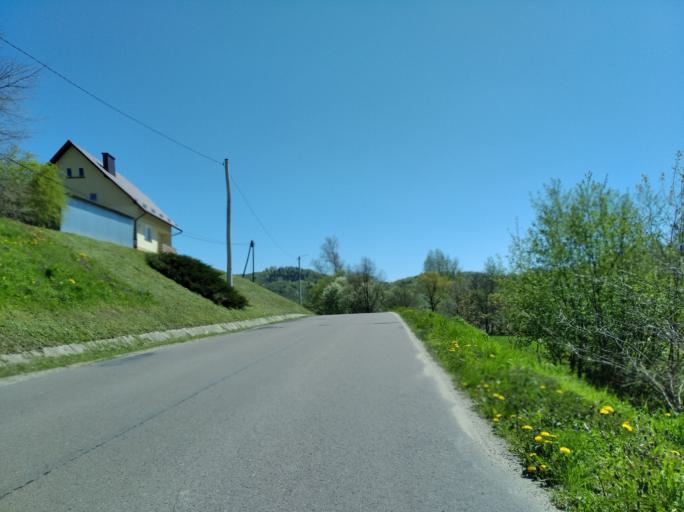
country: PL
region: Subcarpathian Voivodeship
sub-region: Powiat debicki
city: Brzostek
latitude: 49.9177
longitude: 21.4044
